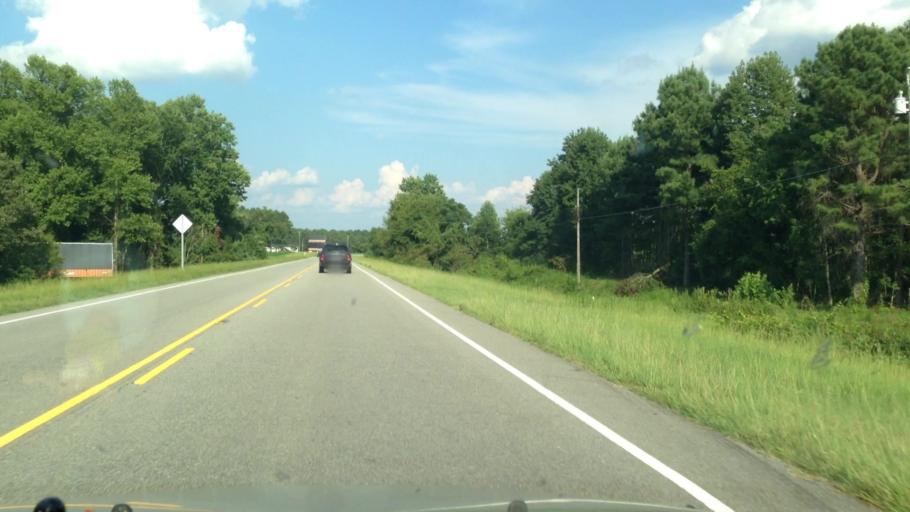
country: US
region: North Carolina
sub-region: Harnett County
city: Lillington
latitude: 35.4183
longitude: -78.8853
